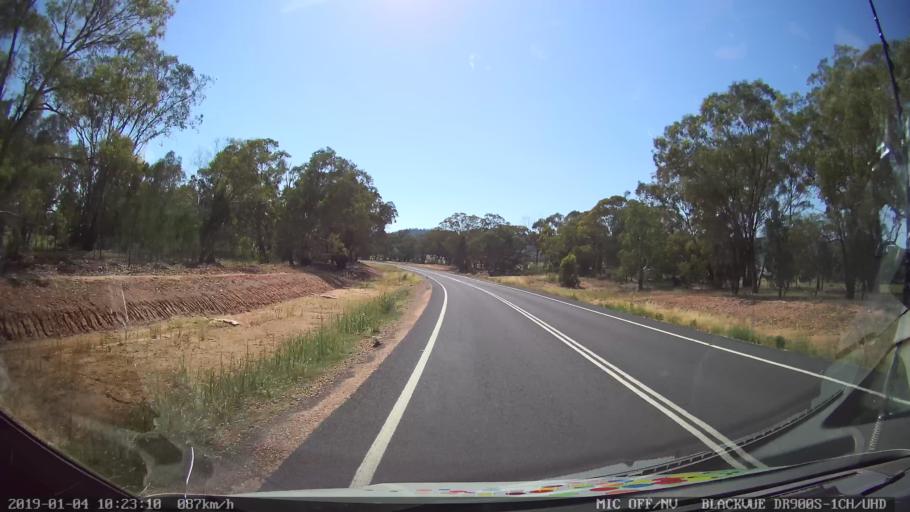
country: AU
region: New South Wales
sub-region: Cabonne
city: Canowindra
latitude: -33.3718
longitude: 148.5355
